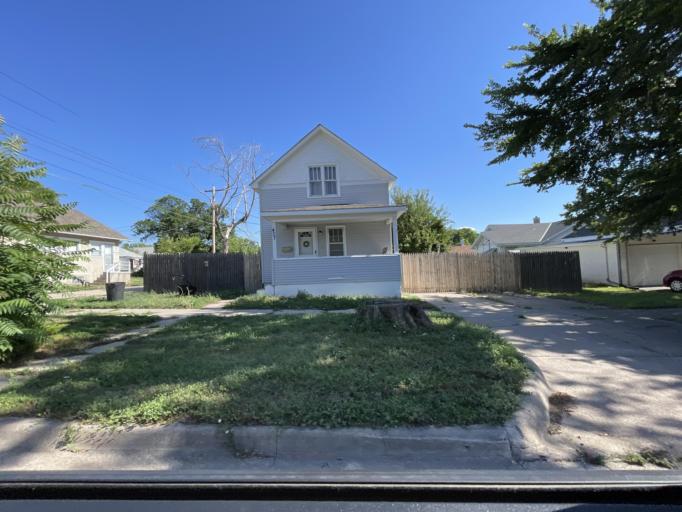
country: US
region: Nebraska
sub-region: Red Willow County
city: McCook
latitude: 40.2047
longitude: -100.6207
